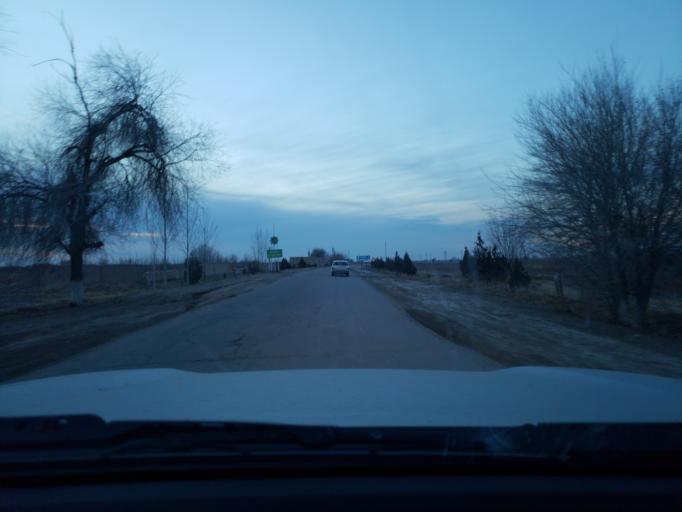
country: TM
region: Dasoguz
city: Tagta
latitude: 41.5857
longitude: 60.0537
